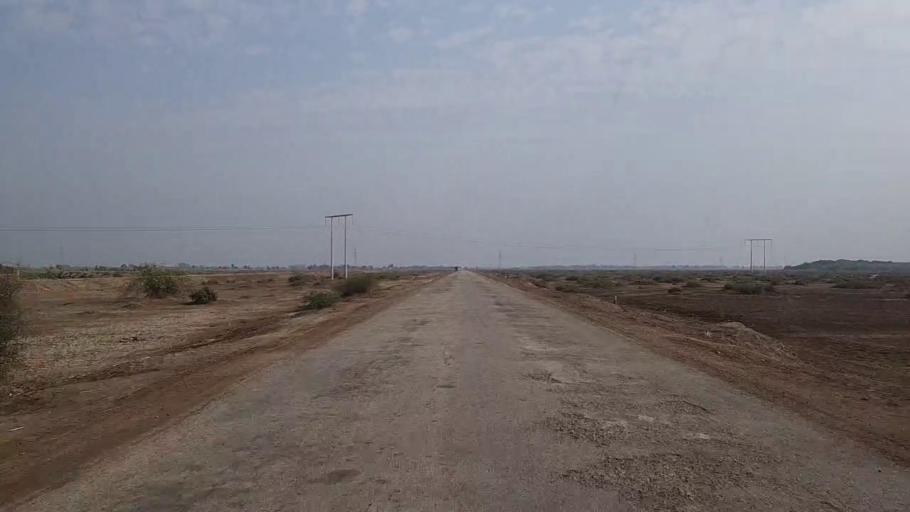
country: PK
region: Sindh
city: Mirpur Khas
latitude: 25.4245
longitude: 69.0208
